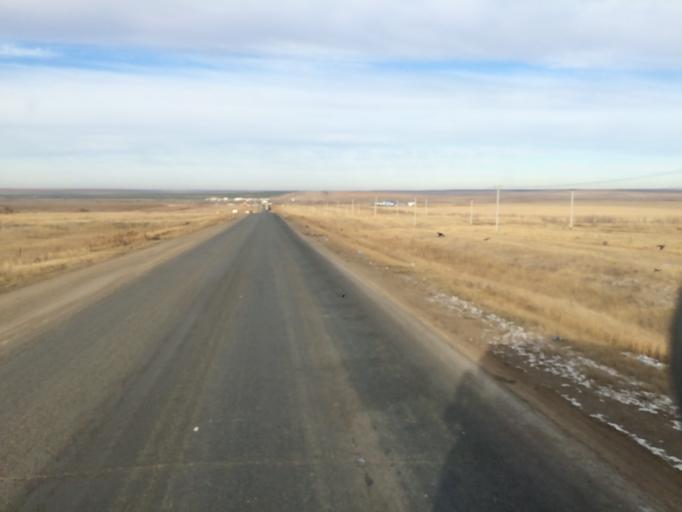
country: KZ
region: Batys Qazaqstan
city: Peremetnoe
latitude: 51.6541
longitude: 51.0102
